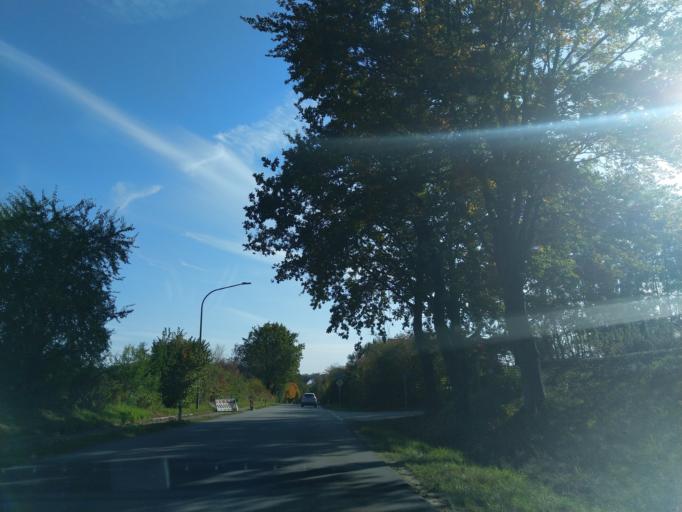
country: DE
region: Bavaria
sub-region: Lower Bavaria
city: Metten
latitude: 48.8882
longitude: 12.9247
